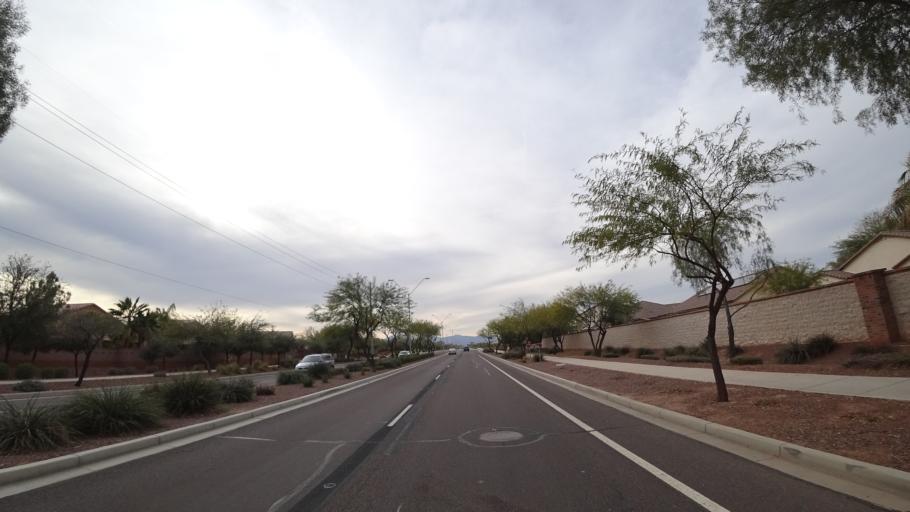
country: US
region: Arizona
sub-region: Maricopa County
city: El Mirage
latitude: 33.5948
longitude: -112.3661
